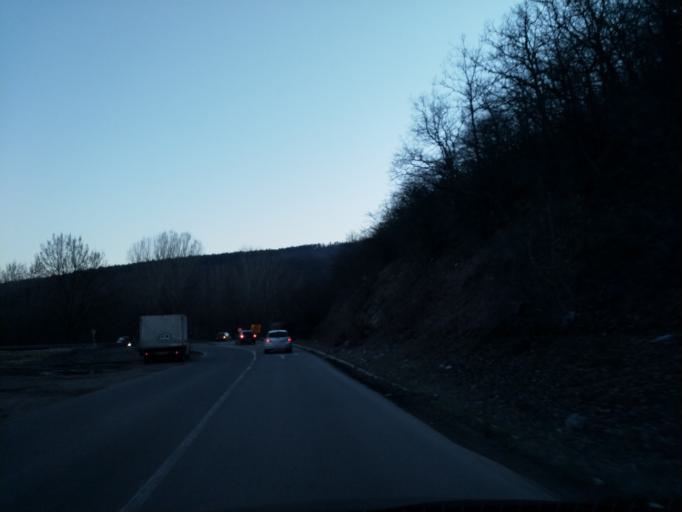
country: RS
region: Central Serbia
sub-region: Pomoravski Okrug
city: Paracin
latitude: 43.8679
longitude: 21.4696
